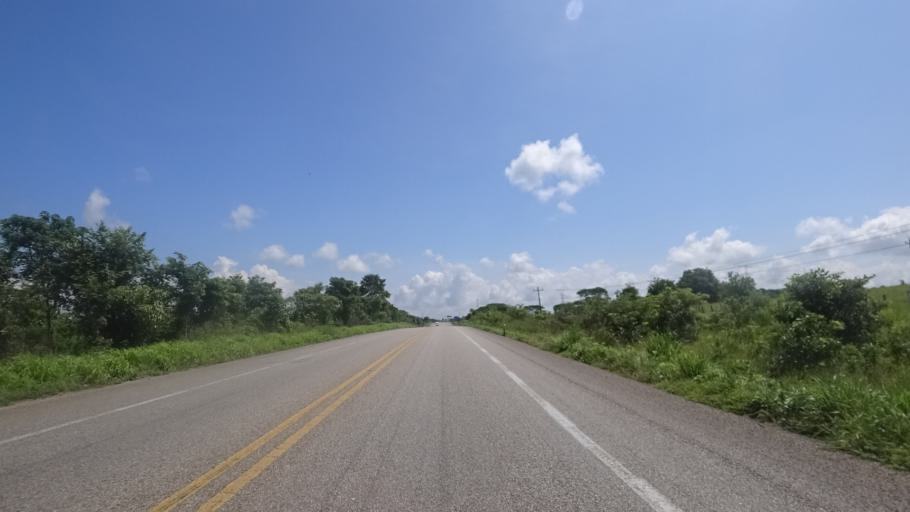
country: MX
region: Chiapas
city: Emiliano Zapata
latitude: 17.7705
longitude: -91.8376
